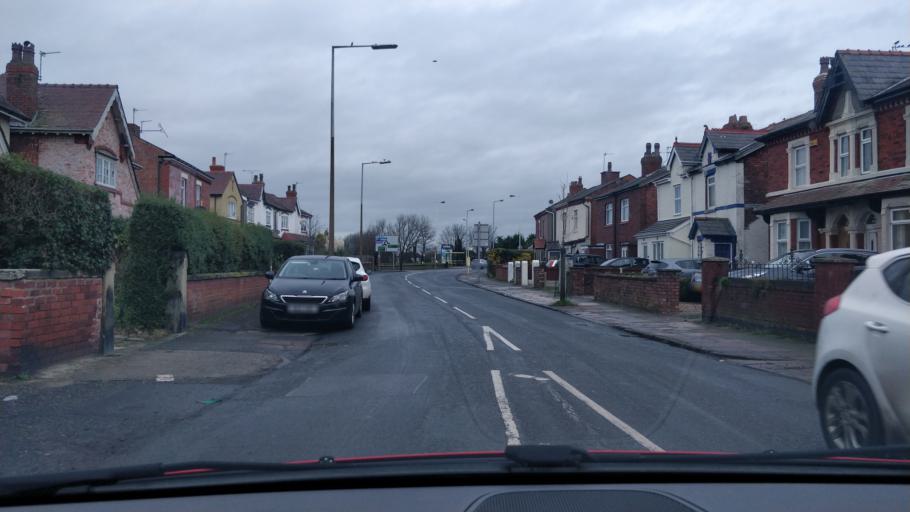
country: GB
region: England
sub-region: Lancashire
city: Banks
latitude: 53.6744
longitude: -2.9482
